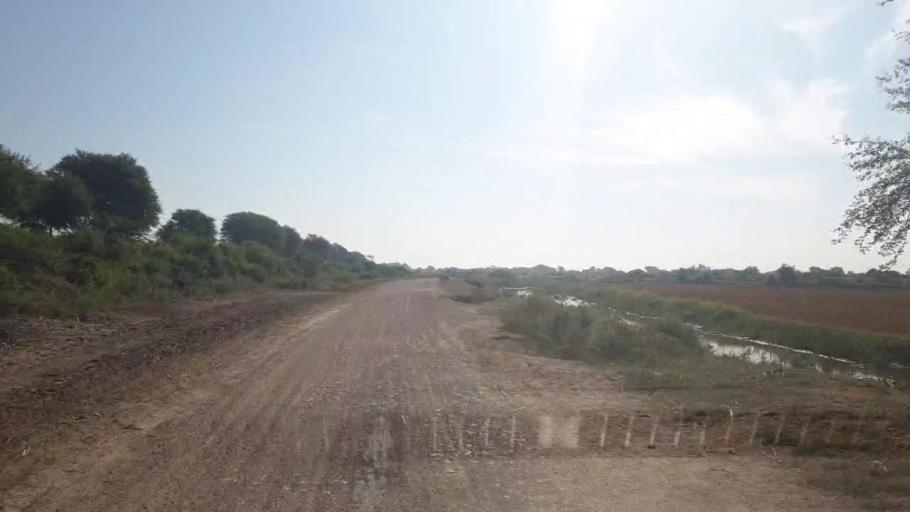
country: PK
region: Sindh
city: Rajo Khanani
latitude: 24.9703
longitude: 68.7928
